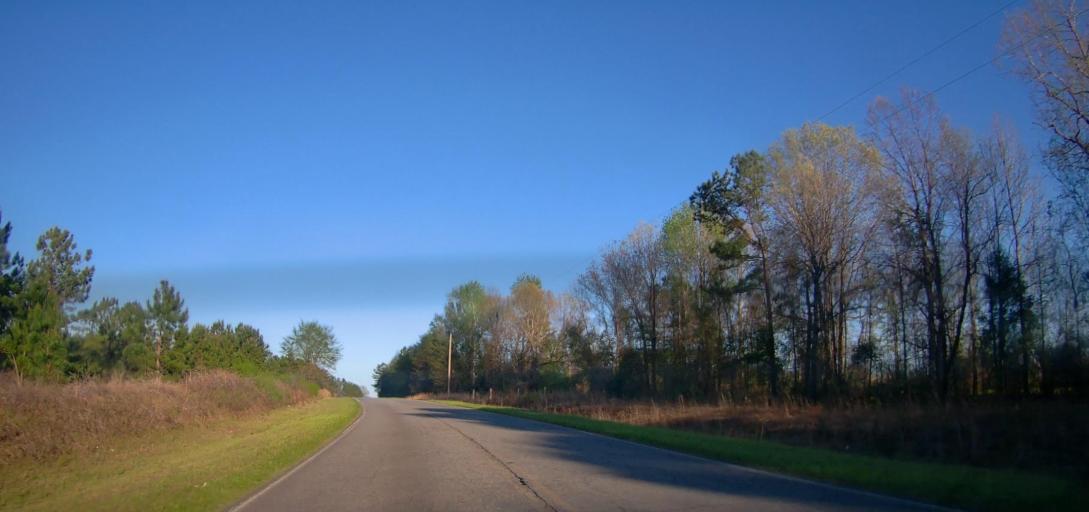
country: US
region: Georgia
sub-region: Wilkinson County
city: Gordon
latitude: 32.8710
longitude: -83.2427
